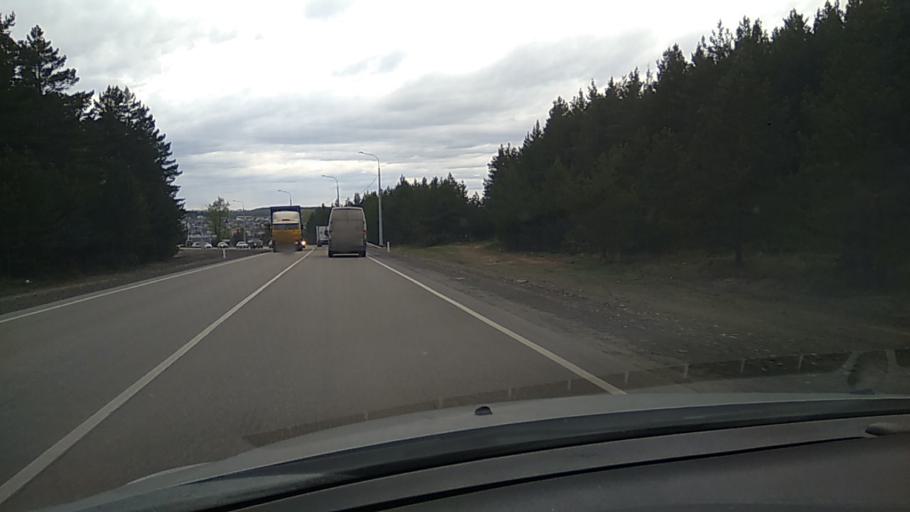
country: RU
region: Sverdlovsk
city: Dvurechensk
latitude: 56.6324
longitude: 61.2647
